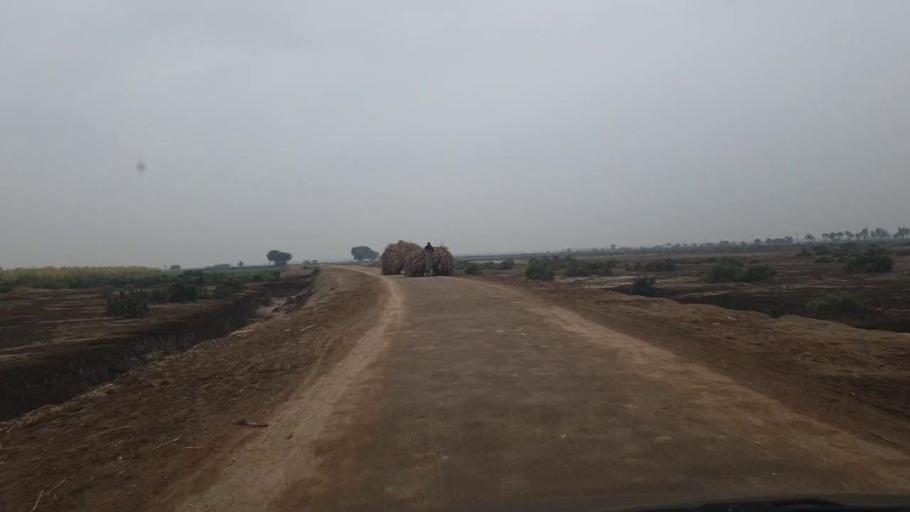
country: PK
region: Sindh
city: Tando Adam
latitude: 25.8275
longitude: 68.6997
